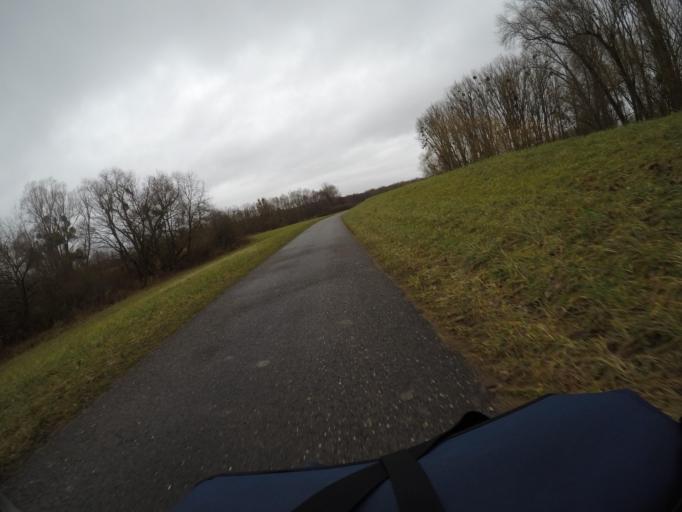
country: DE
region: Rheinland-Pfalz
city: Leimersheim
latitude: 49.1391
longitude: 8.3570
